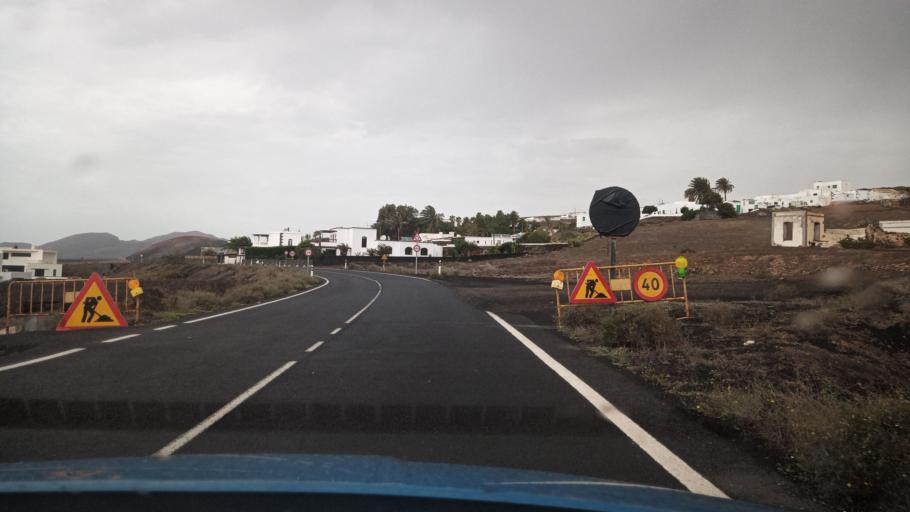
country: ES
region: Canary Islands
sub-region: Provincia de Las Palmas
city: Yaiza
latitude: 28.9455
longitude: -13.7391
